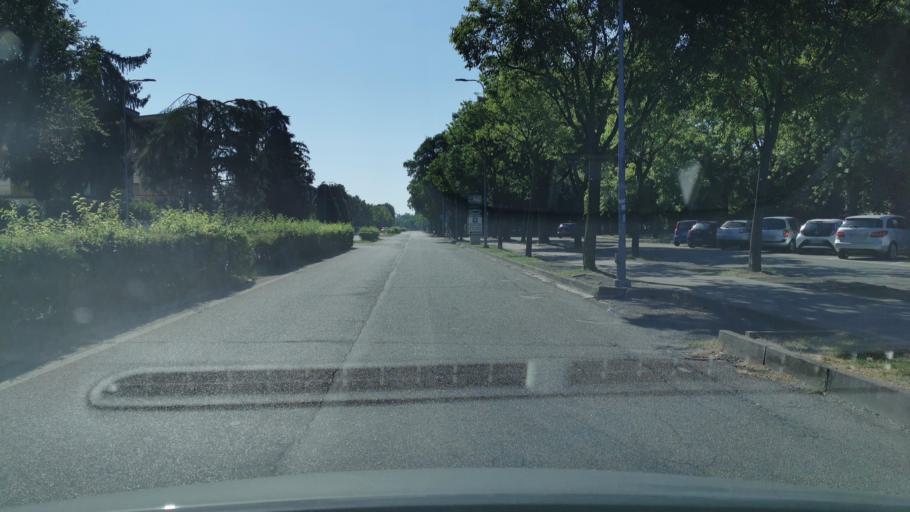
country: IT
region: Emilia-Romagna
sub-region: Provincia di Modena
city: Carpi Centro
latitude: 44.7841
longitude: 10.8712
